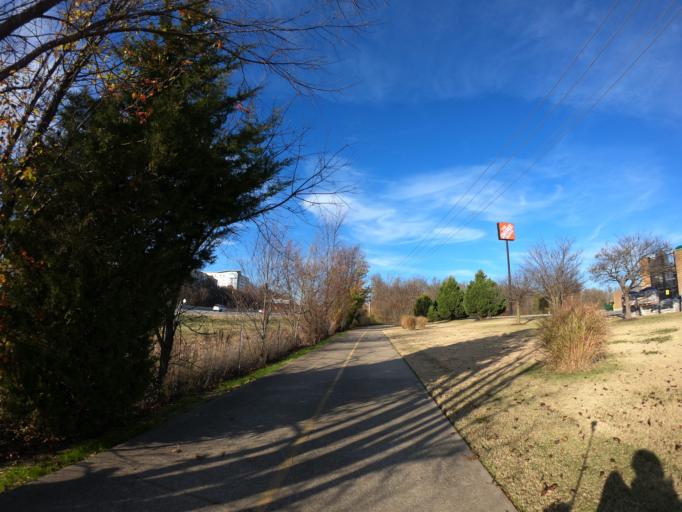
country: US
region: Arkansas
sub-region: Benton County
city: Bentonville
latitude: 36.3177
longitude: -94.1845
